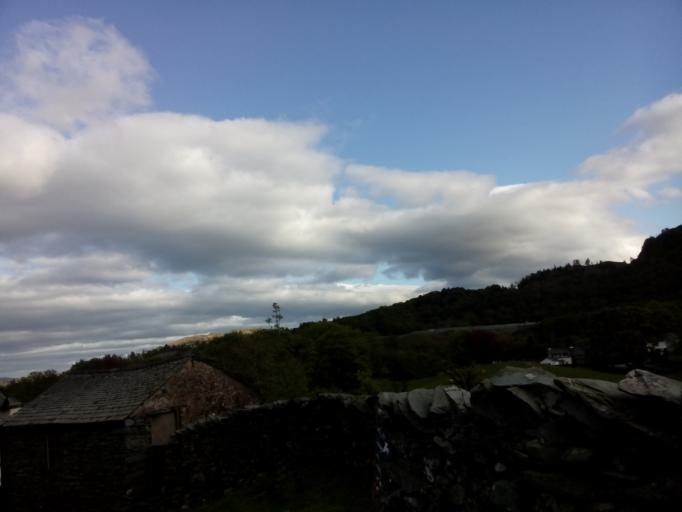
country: GB
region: England
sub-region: Cumbria
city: Ambleside
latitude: 54.4404
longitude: -3.0506
